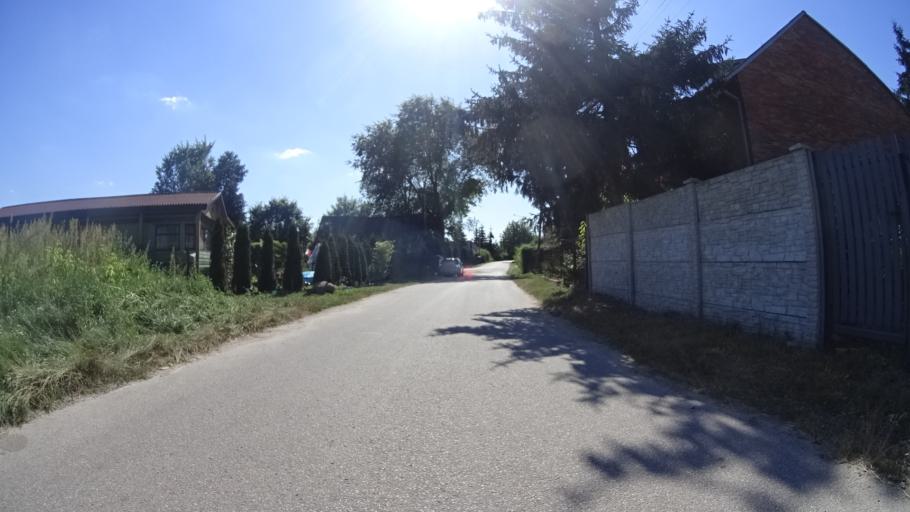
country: PL
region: Masovian Voivodeship
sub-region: Powiat bialobrzeski
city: Wysmierzyce
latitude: 51.6565
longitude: 20.8270
